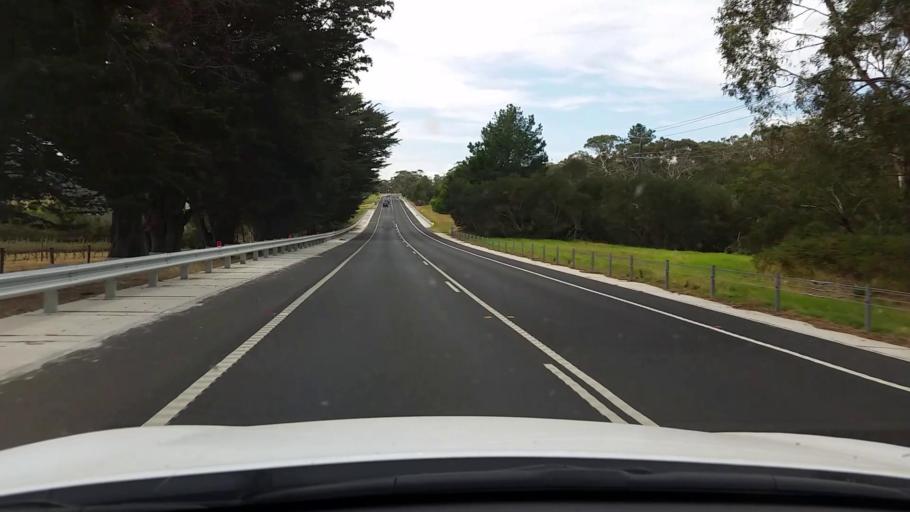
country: AU
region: Victoria
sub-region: Mornington Peninsula
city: Safety Beach
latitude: -38.3202
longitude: 145.0152
